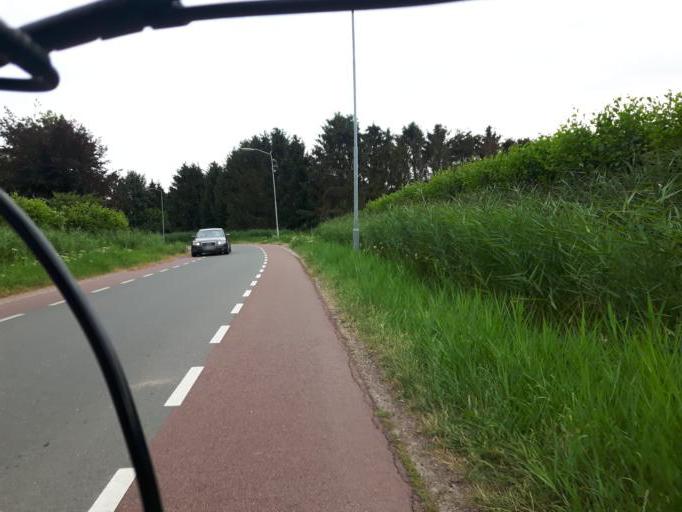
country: NL
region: Gelderland
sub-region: Gemeente Maasdriel
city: Heerewaarden
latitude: 51.8707
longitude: 5.3729
